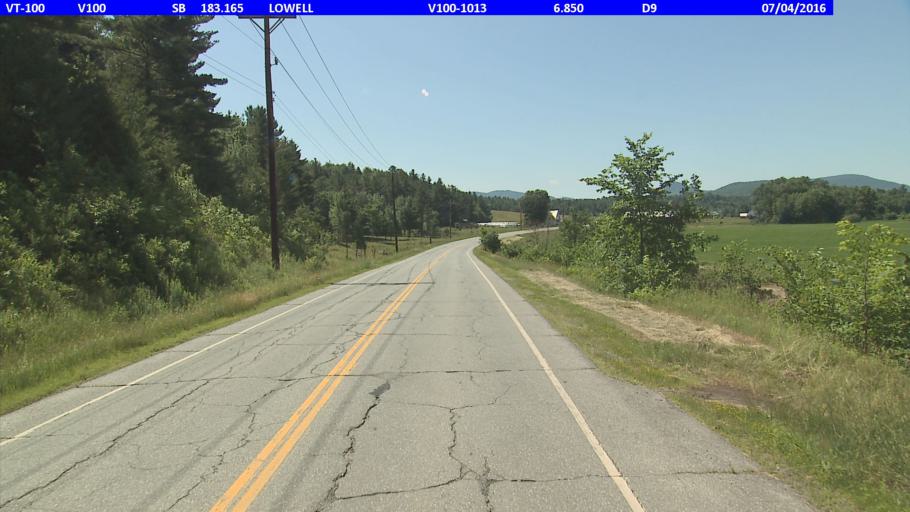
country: US
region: Vermont
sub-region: Orleans County
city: Newport
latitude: 44.8324
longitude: -72.4325
